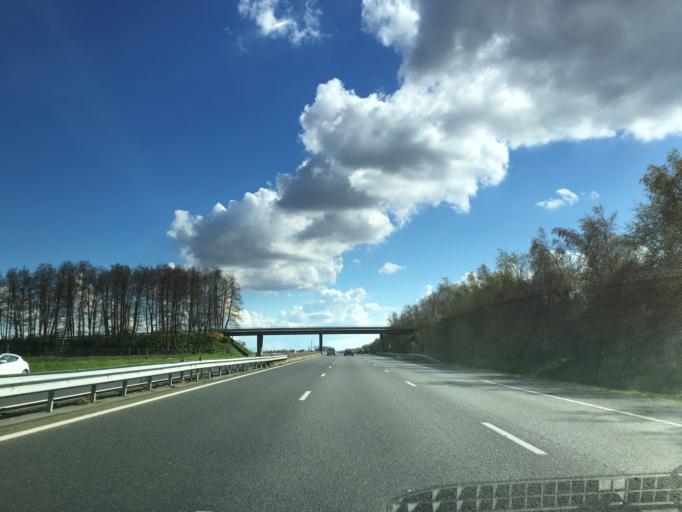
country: FR
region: Nord-Pas-de-Calais
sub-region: Departement du Pas-de-Calais
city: Vaulx-Vraucourt
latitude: 50.1609
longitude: 2.8734
